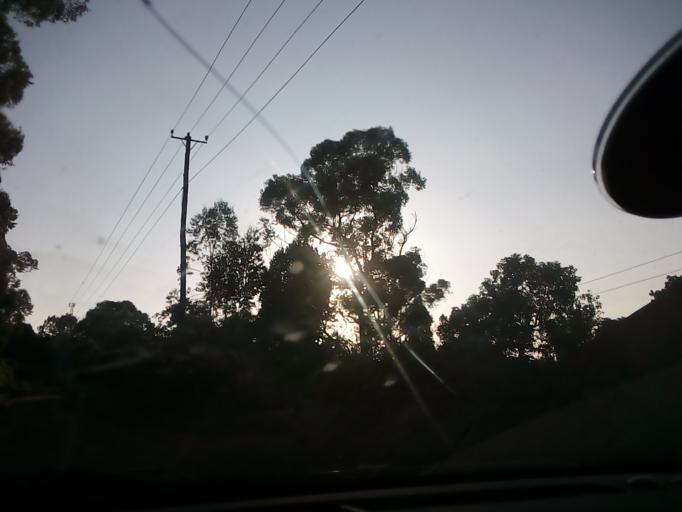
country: UG
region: Central Region
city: Masaka
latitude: -0.3419
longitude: 31.7594
